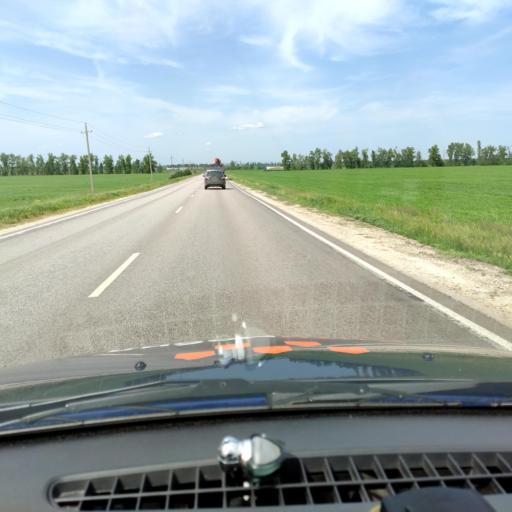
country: RU
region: Voronezj
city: Novaya Usman'
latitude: 51.5609
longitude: 39.3761
